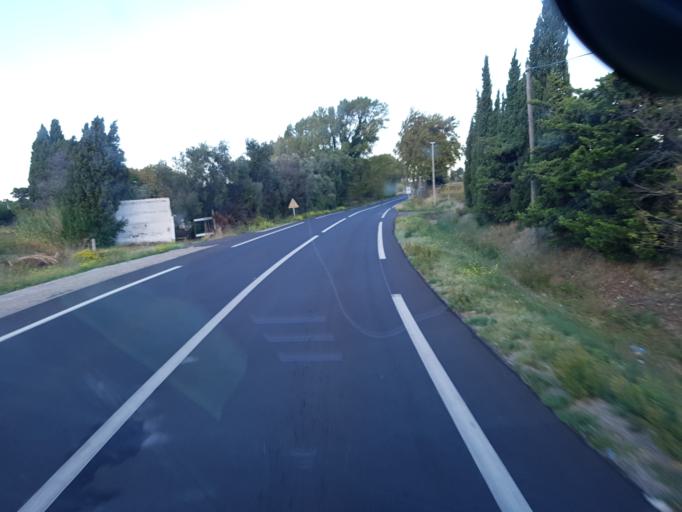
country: FR
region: Languedoc-Roussillon
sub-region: Departement de l'Aude
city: Leucate
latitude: 42.9605
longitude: 2.9869
